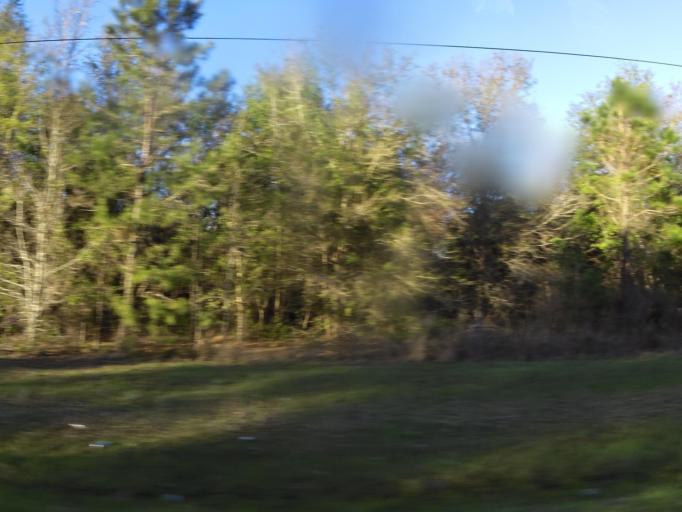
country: US
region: Florida
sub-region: Clay County
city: Keystone Heights
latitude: 29.8461
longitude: -82.0790
